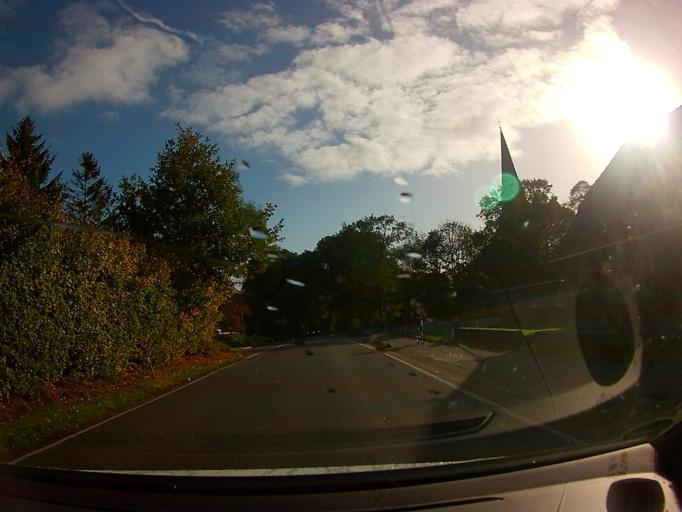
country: DE
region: Schleswig-Holstein
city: Breklum
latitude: 54.6094
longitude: 8.9922
